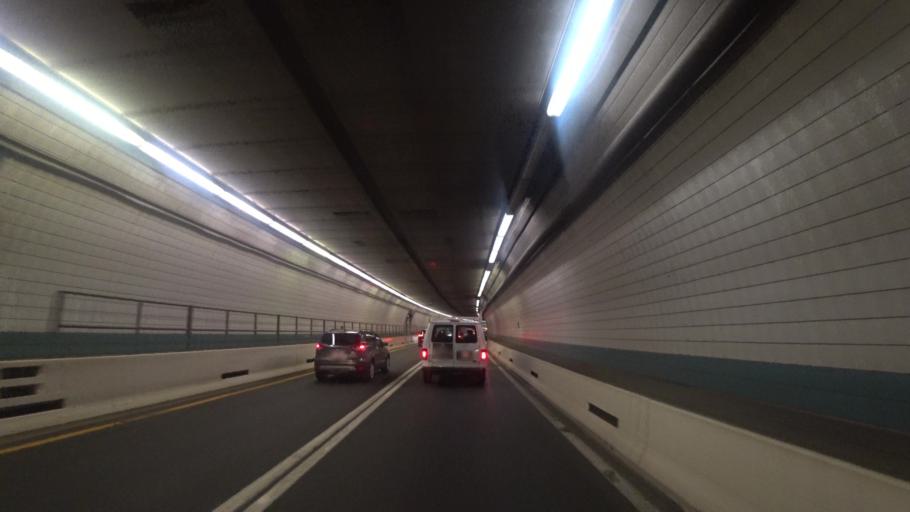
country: US
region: Massachusetts
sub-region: Suffolk County
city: South Boston
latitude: 42.3494
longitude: -71.0366
